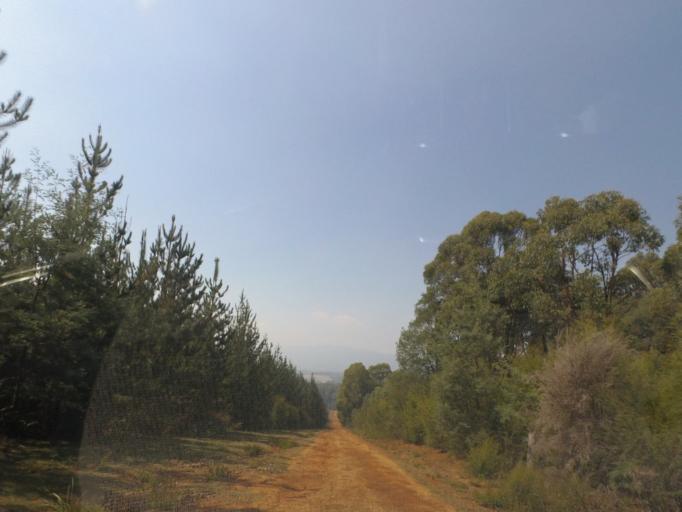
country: AU
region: Victoria
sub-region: Yarra Ranges
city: Healesville
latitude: -37.5594
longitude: 145.6371
